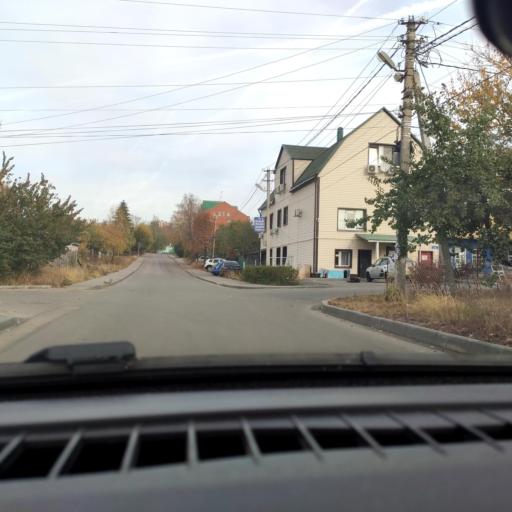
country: RU
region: Voronezj
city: Voronezh
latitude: 51.6956
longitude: 39.1748
